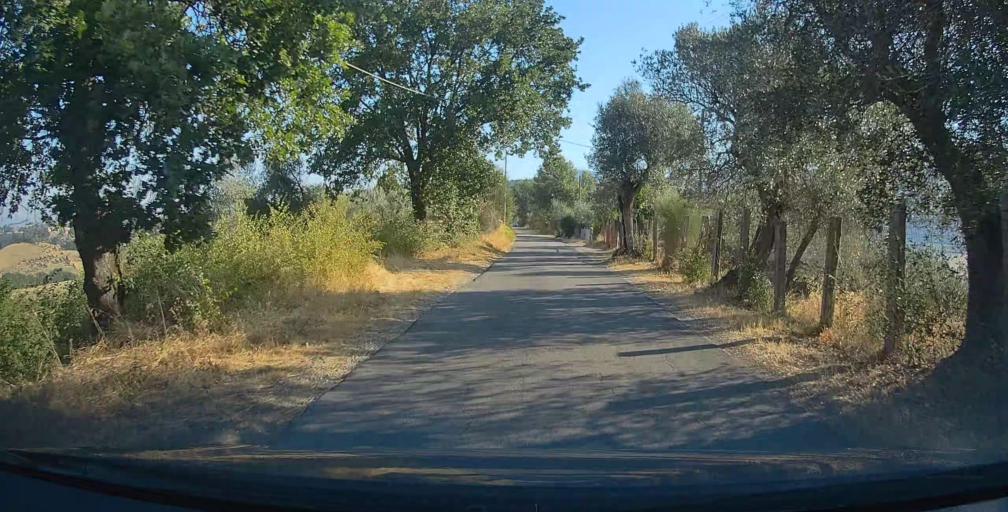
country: IT
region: Umbria
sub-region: Provincia di Terni
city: Calvi dell'Umbria
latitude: 42.3774
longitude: 12.5674
